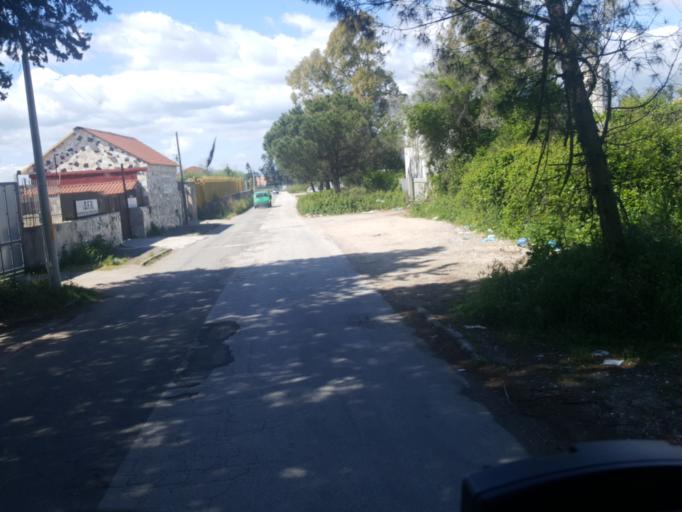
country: IT
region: Campania
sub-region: Provincia di Napoli
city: Torretta-Scalzapecora
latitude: 40.9328
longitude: 14.1062
